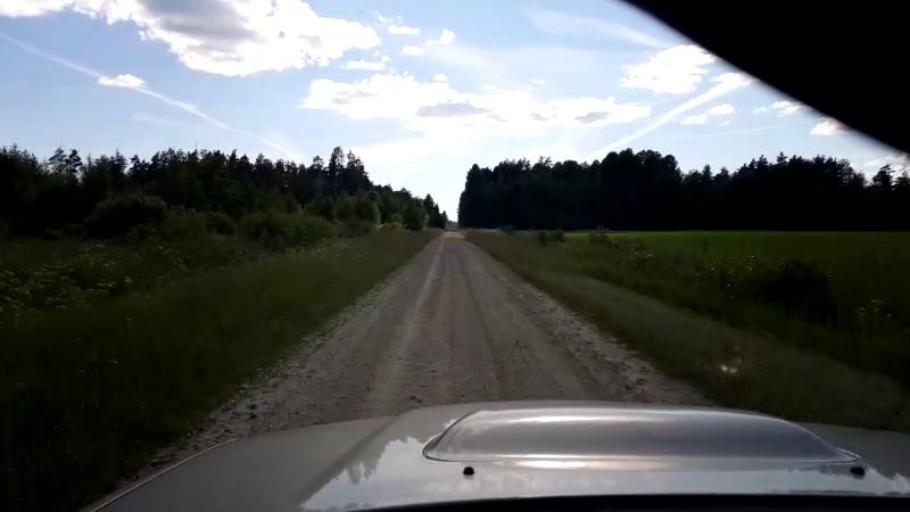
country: EE
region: Paernumaa
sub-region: Sindi linn
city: Sindi
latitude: 58.4937
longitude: 24.6156
